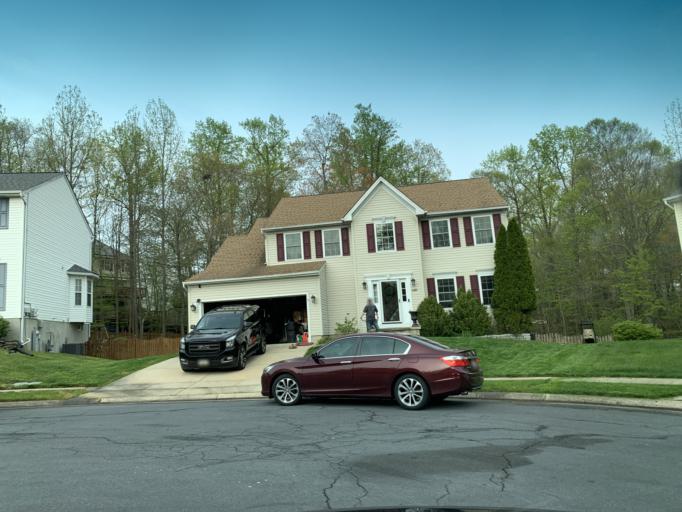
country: US
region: Maryland
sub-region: Harford County
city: Riverside
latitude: 39.4743
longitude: -76.2553
